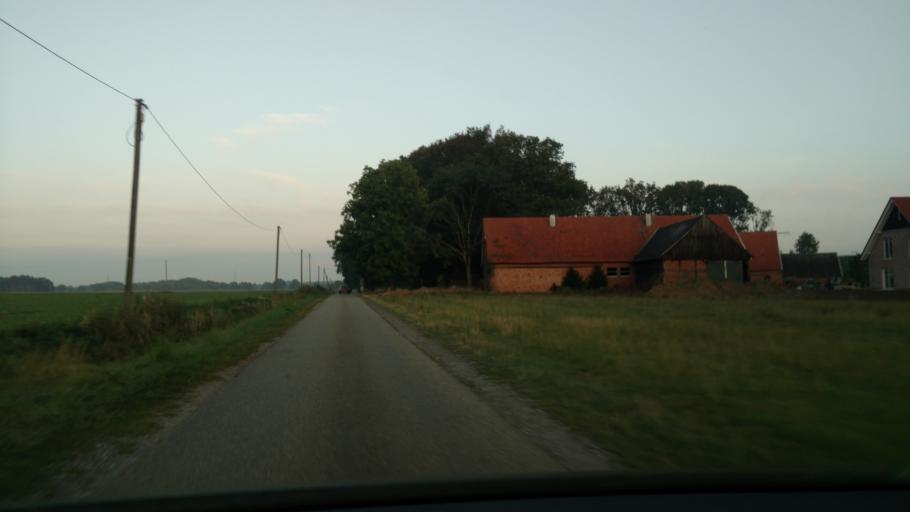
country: DE
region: North Rhine-Westphalia
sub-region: Regierungsbezirk Munster
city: Velen
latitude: 51.8577
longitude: 6.9914
